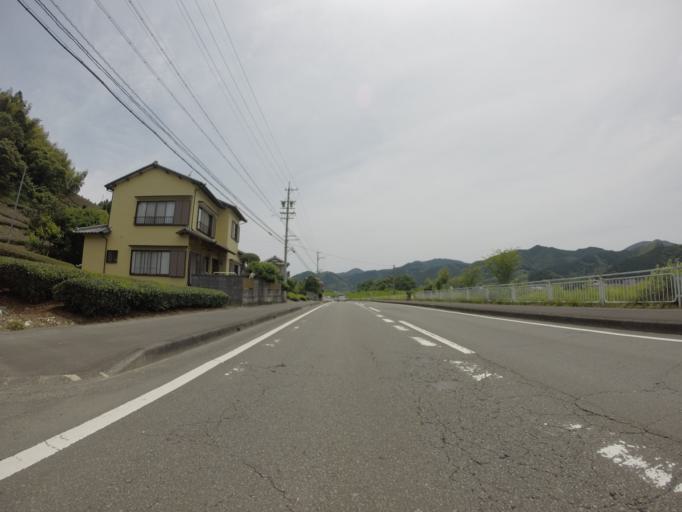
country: JP
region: Shizuoka
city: Shizuoka-shi
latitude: 34.9888
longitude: 138.3025
